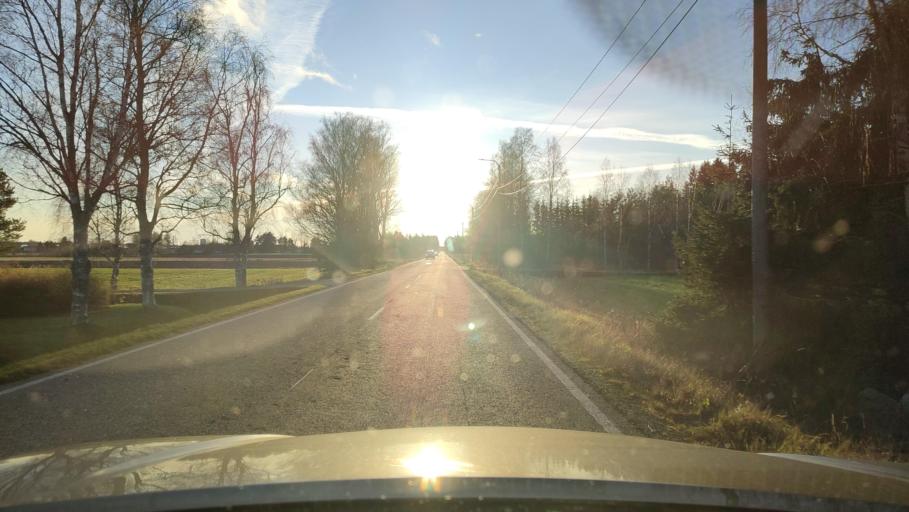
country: FI
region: Ostrobothnia
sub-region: Vaasa
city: Malax
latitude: 62.7032
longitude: 21.5907
